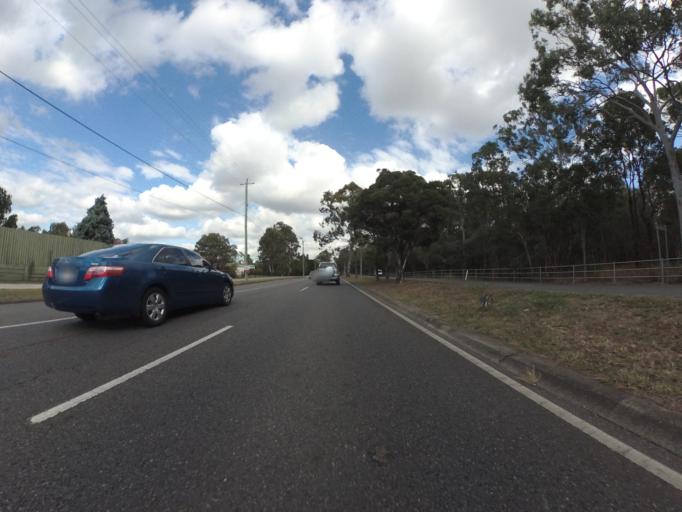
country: AU
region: Queensland
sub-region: Brisbane
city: Wynnum West
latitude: -27.4674
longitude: 153.1393
